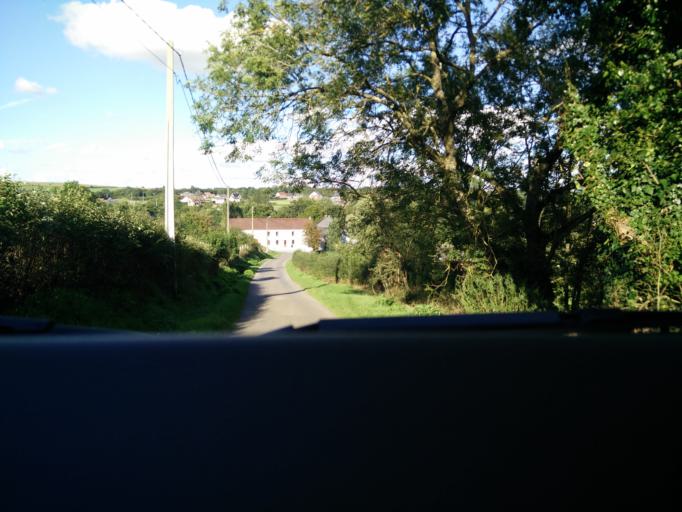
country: BE
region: Wallonia
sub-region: Province du Hainaut
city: Beaumont
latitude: 50.1848
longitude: 4.2638
